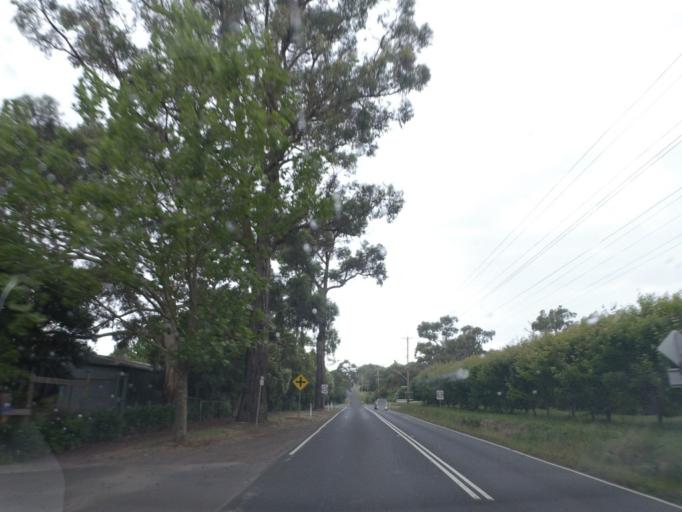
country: AU
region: Victoria
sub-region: Yarra Ranges
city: Mount Evelyn
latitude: -37.7823
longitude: 145.4175
